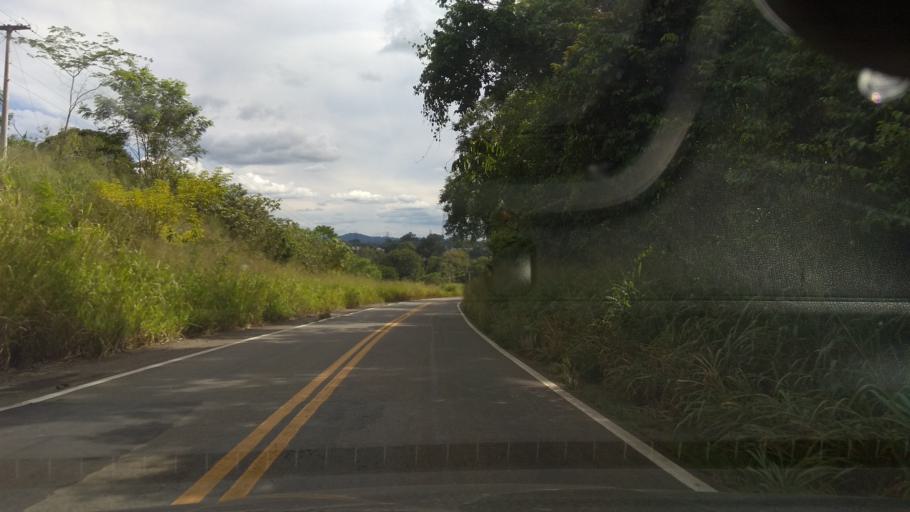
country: BR
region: Bahia
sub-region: Ubata
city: Ubata
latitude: -14.2305
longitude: -39.4528
